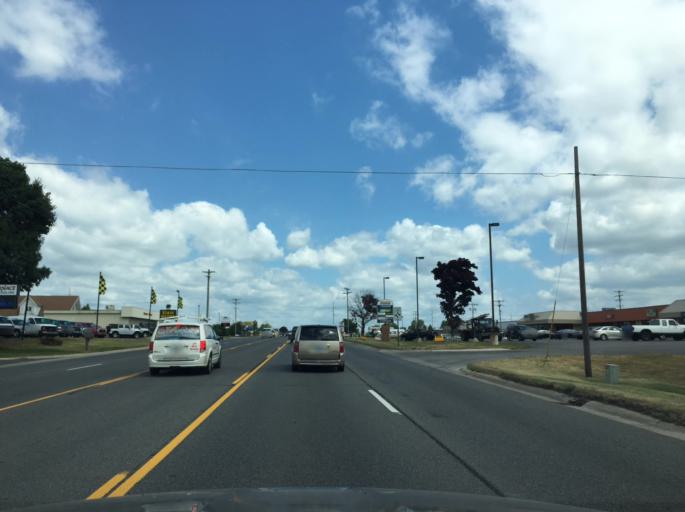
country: US
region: Michigan
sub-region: Grand Traverse County
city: Traverse City
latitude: 44.6753
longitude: -85.6563
